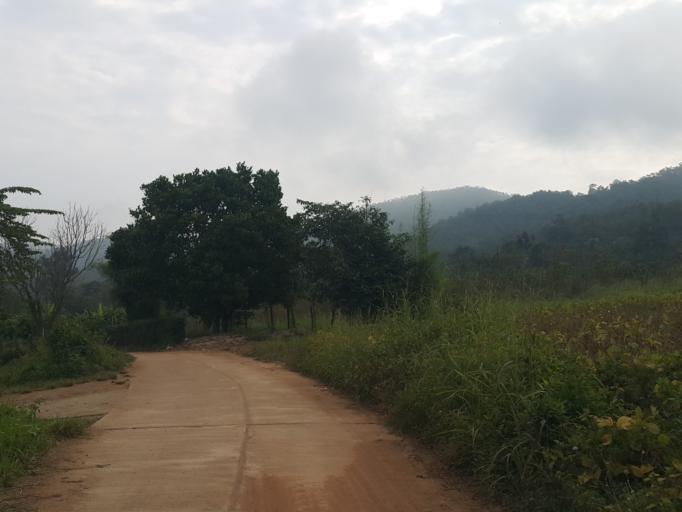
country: TH
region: Mae Hong Son
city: Wiang Nuea
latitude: 19.3784
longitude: 98.4571
